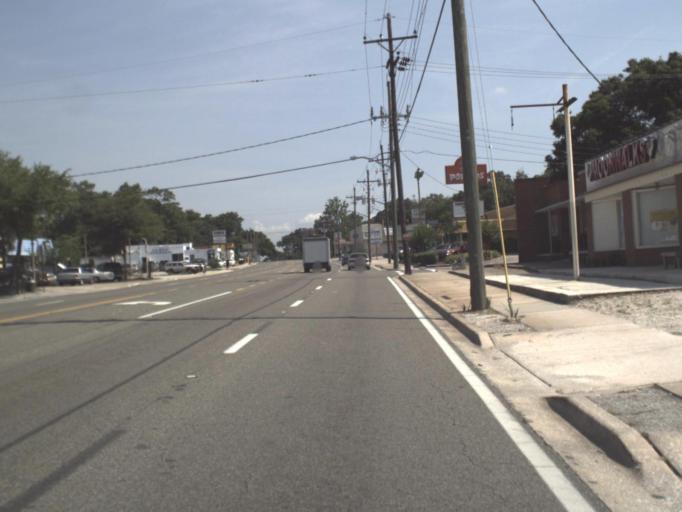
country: US
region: Florida
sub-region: Duval County
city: Jacksonville
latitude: 30.3353
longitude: -81.6026
